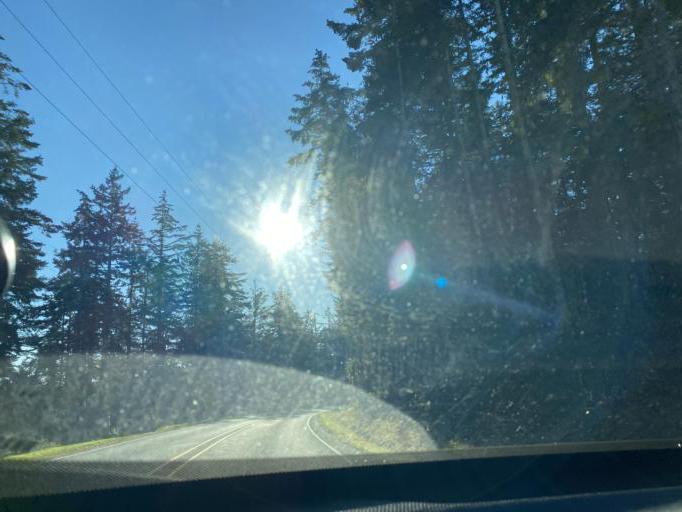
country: US
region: Washington
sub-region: Island County
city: Camano
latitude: 48.1149
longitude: -122.5608
